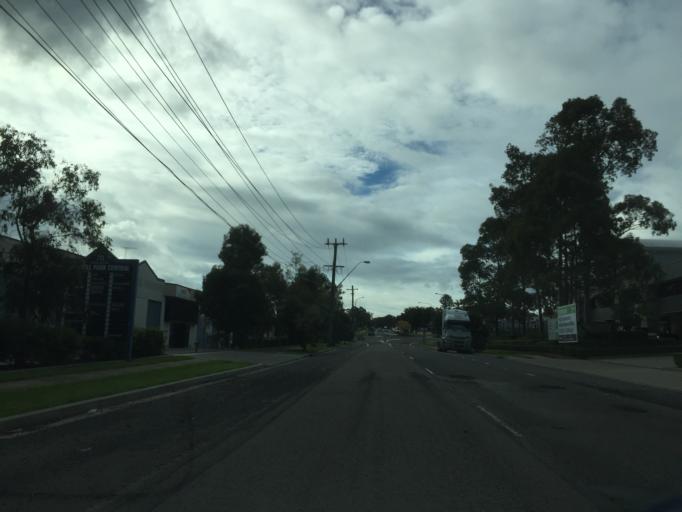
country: AU
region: New South Wales
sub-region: Blacktown
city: Doonside
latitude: -33.7916
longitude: 150.8902
